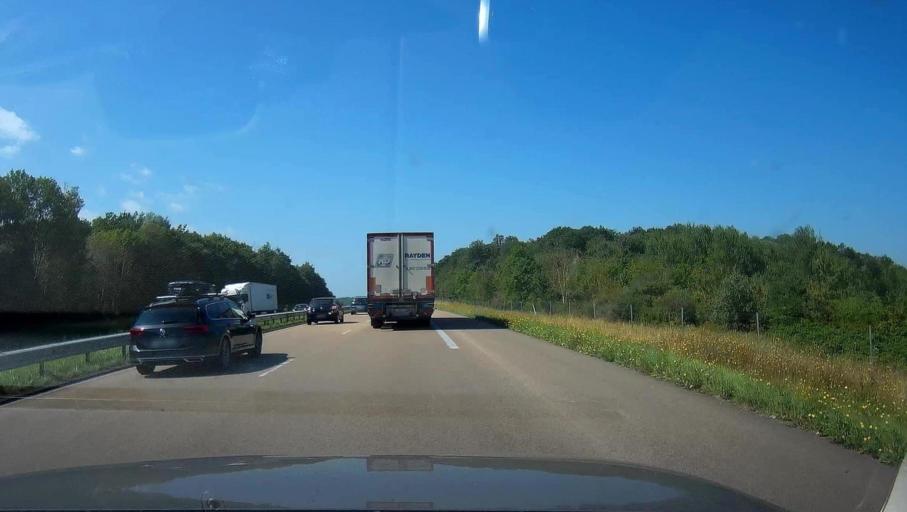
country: FR
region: Champagne-Ardenne
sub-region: Departement de l'Aube
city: Bar-sur-Seine
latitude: 48.1805
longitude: 4.3836
